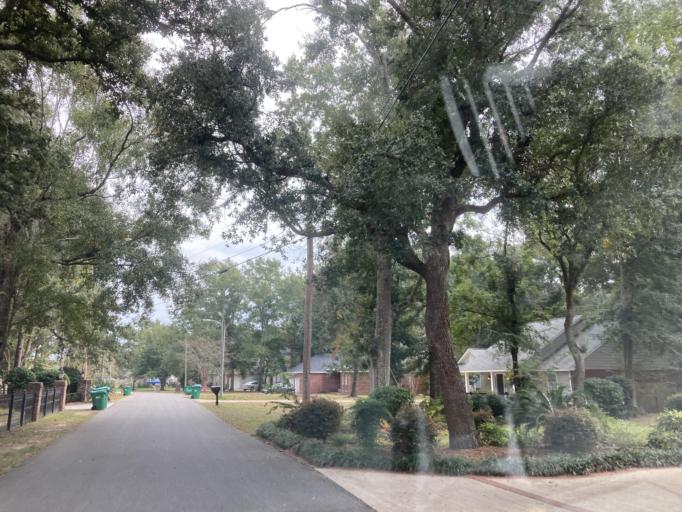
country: US
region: Mississippi
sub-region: Jackson County
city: Gulf Hills
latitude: 30.4407
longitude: -88.8398
